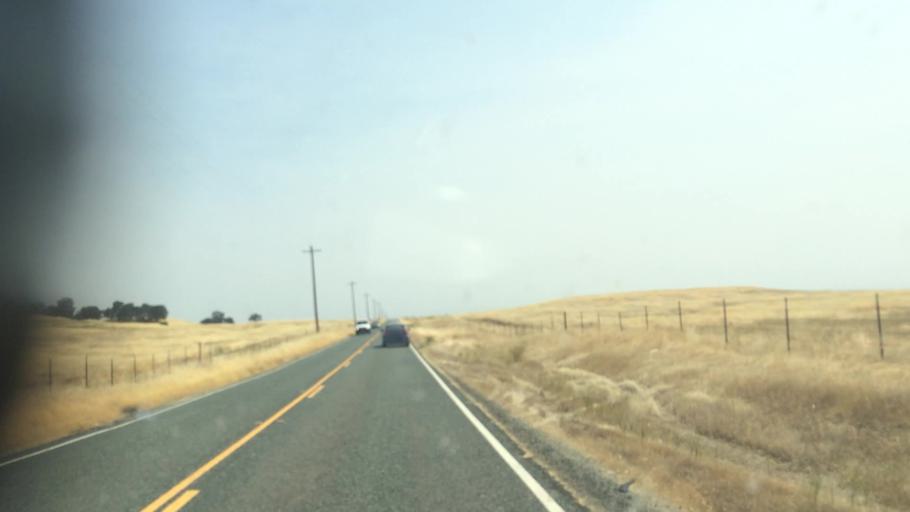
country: US
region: California
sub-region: Sacramento County
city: Clay
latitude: 38.3662
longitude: -121.0763
